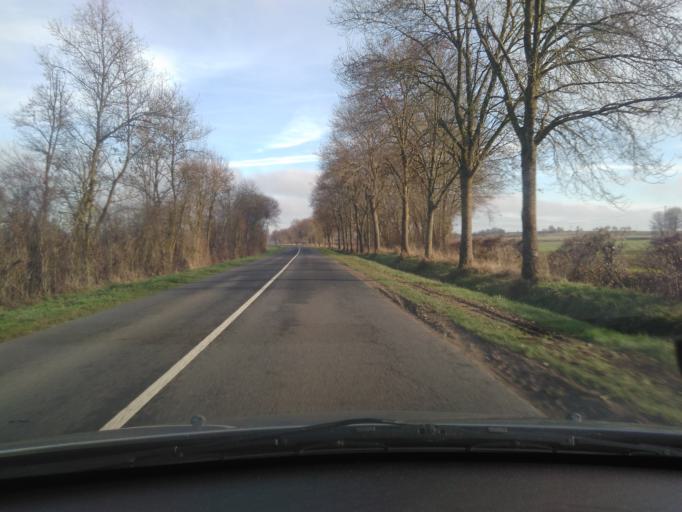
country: FR
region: Centre
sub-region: Departement de l'Indre
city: Montgivray
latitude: 46.6019
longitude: 2.0162
